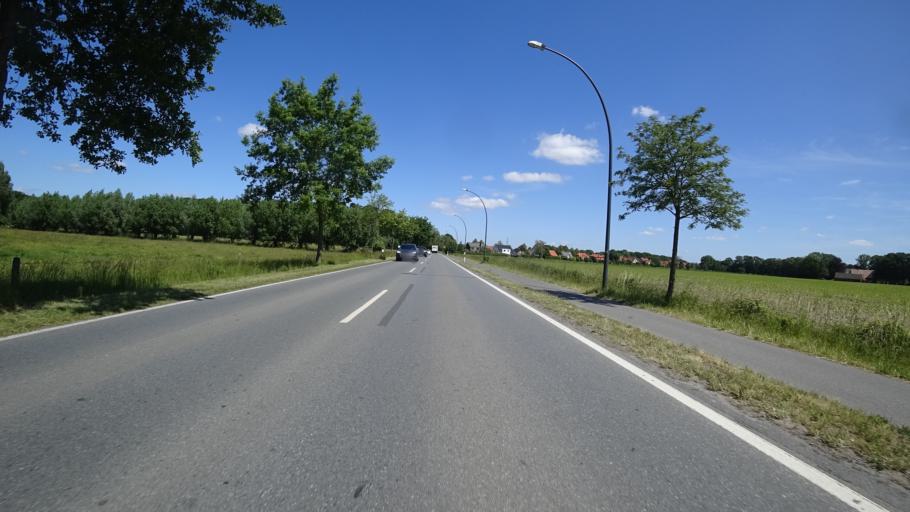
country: DE
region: North Rhine-Westphalia
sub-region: Regierungsbezirk Detmold
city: Guetersloh
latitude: 51.9169
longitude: 8.4281
